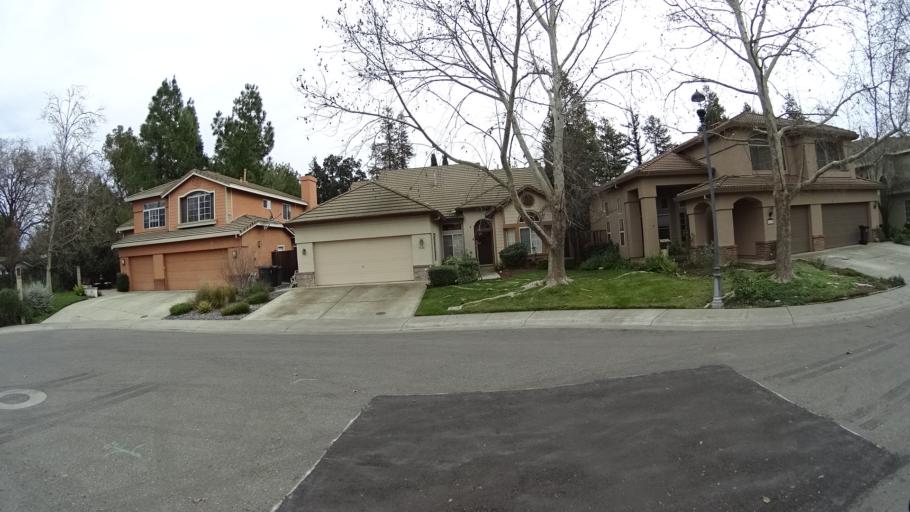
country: US
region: California
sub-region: Yolo County
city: Davis
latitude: 38.5564
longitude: -121.7147
